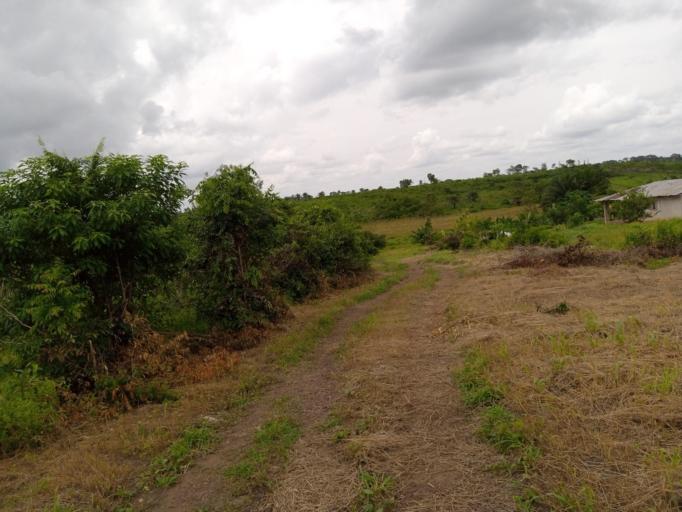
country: SL
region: Southern Province
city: Moyamba
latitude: 8.1654
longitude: -12.4187
